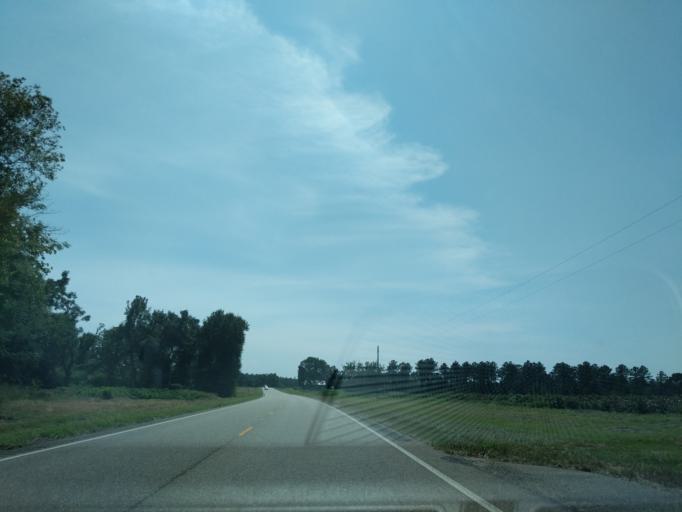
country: US
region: Florida
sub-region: Okaloosa County
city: Crestview
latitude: 31.0191
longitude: -86.6148
